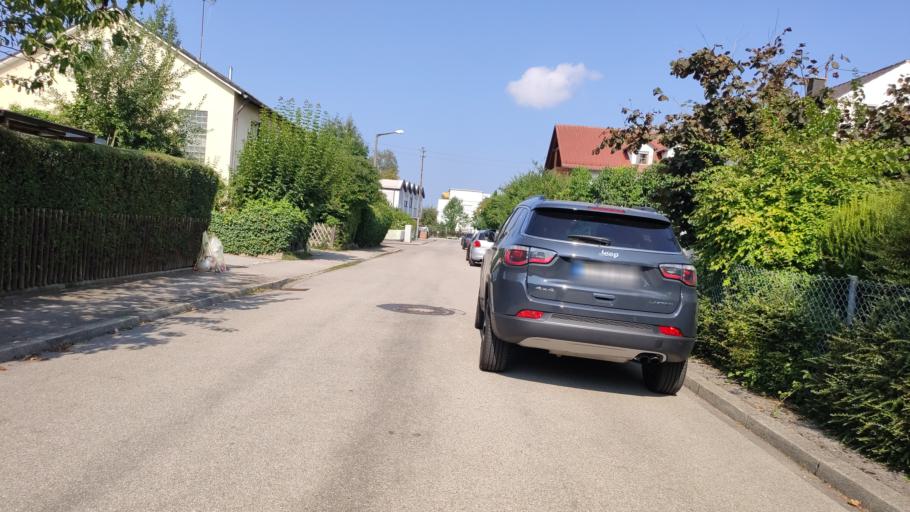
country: DE
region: Bavaria
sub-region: Swabia
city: Bobingen
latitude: 48.2619
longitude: 10.8313
